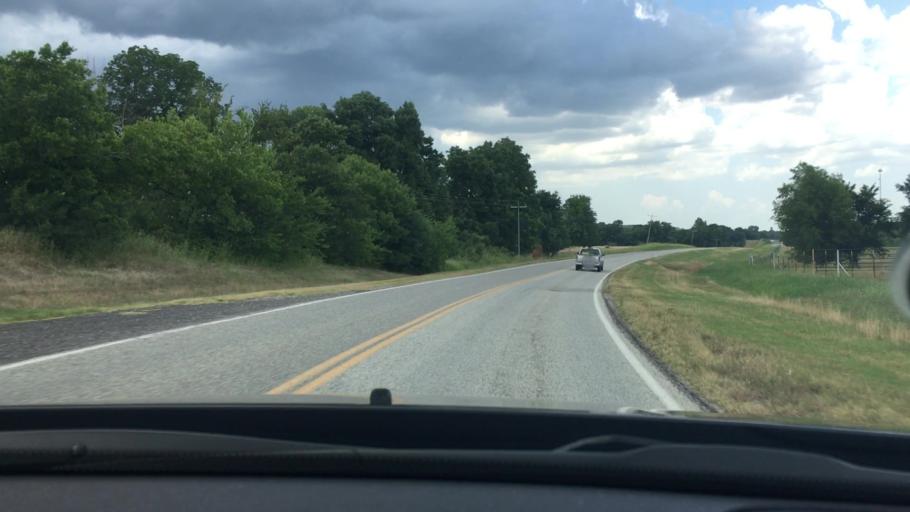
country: US
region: Oklahoma
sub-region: Pontotoc County
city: Ada
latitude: 34.5809
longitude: -96.6345
